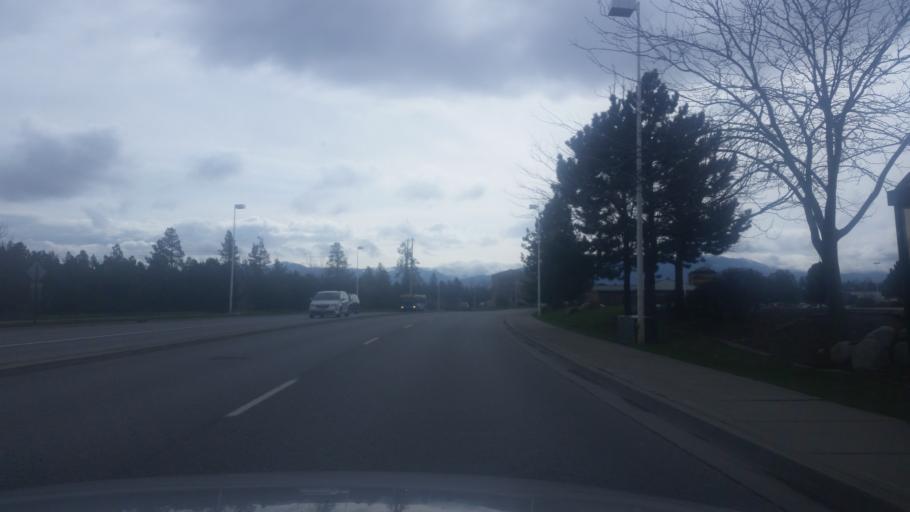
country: US
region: Washington
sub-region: Spokane County
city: Trentwood
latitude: 47.6757
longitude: -117.2057
